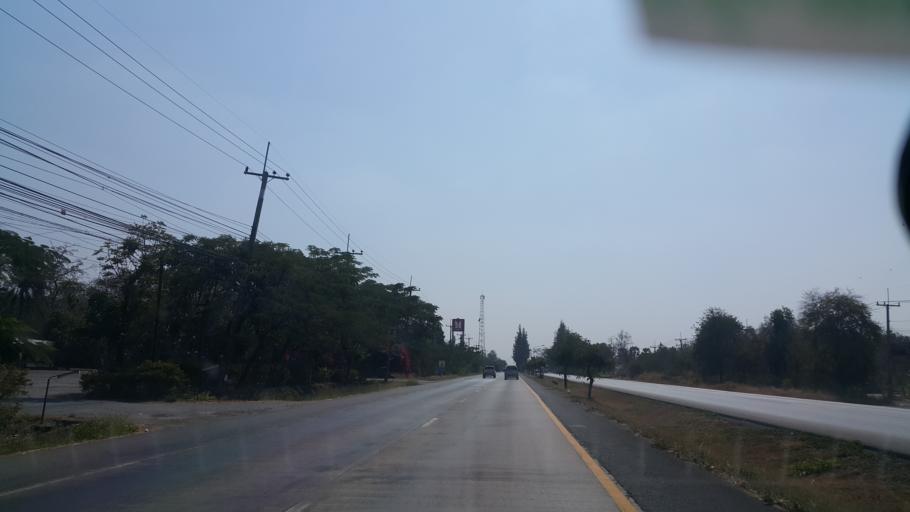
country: TH
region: Nakhon Ratchasima
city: Sida
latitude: 15.5423
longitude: 102.5469
